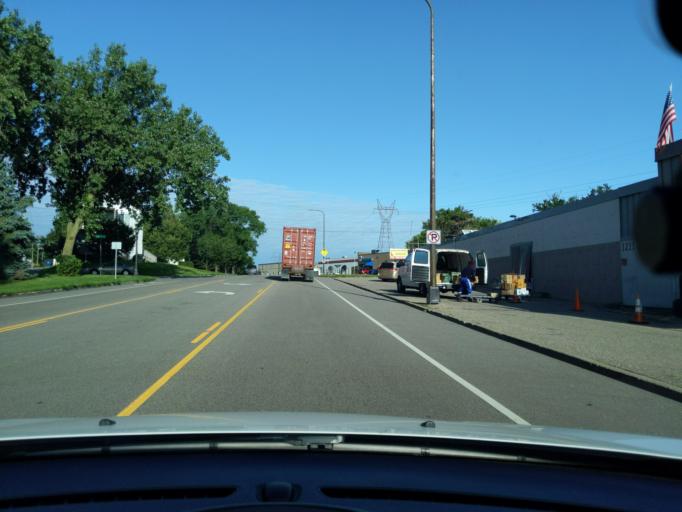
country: US
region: Minnesota
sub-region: Ramsey County
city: Falcon Heights
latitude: 44.9671
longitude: -93.1510
